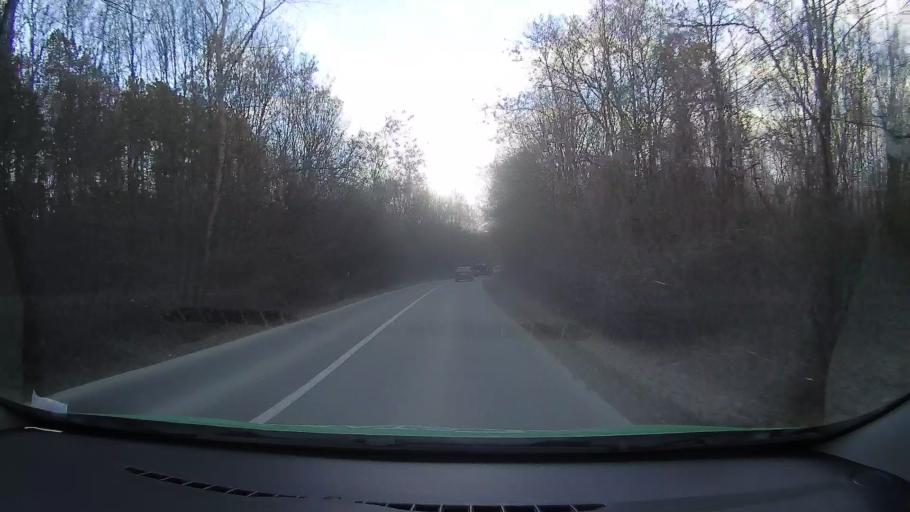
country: RO
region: Dambovita
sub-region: Comuna Gura Ocnitei
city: Gura Ocnitei
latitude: 44.9511
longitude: 25.5958
